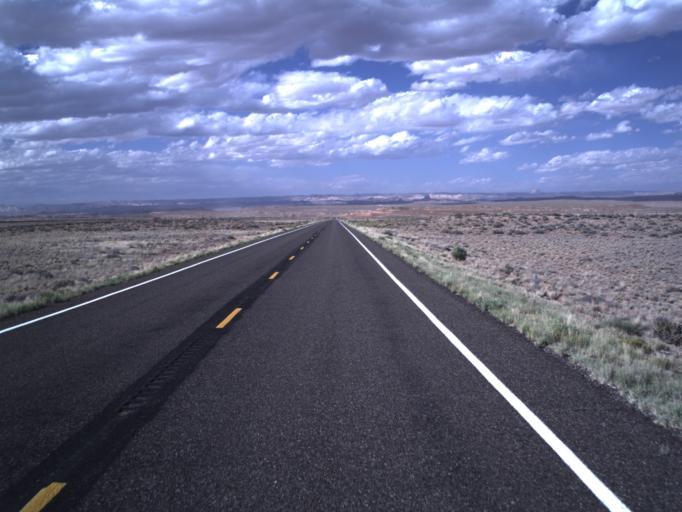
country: US
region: Utah
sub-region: Emery County
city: Ferron
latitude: 38.2824
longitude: -110.6630
